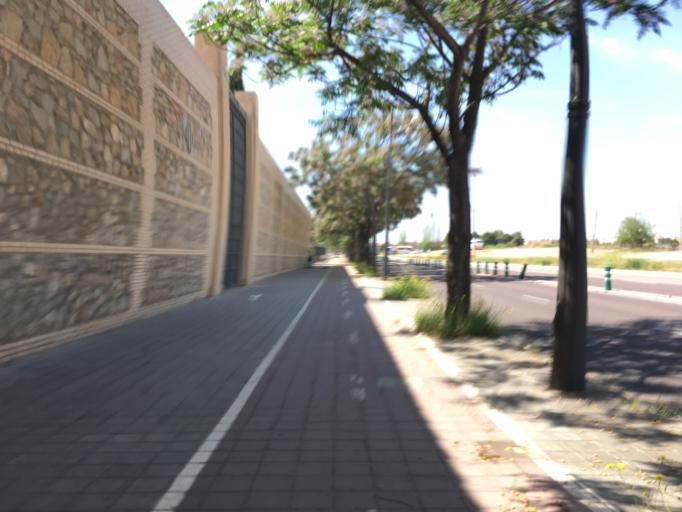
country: ES
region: Valencia
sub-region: Provincia de Valencia
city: Mislata
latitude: 39.4840
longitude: -0.4060
